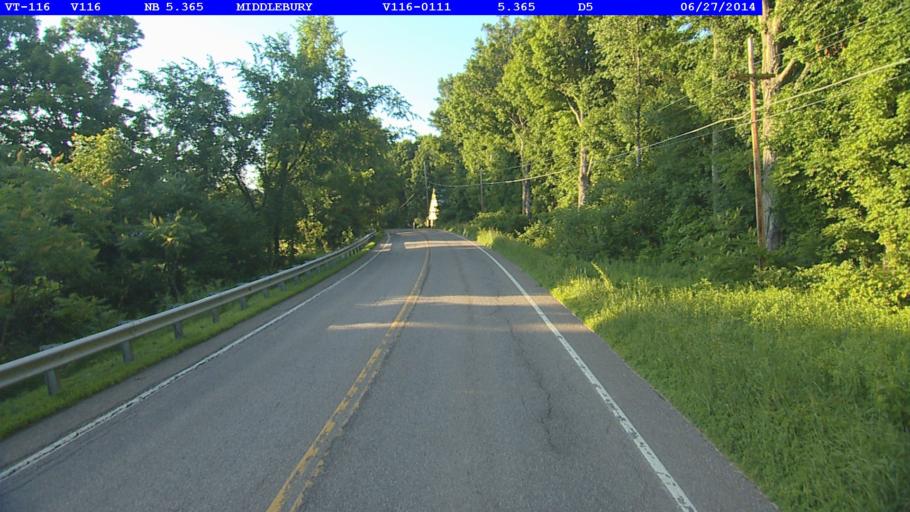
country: US
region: Vermont
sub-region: Addison County
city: Middlebury (village)
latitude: 44.0374
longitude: -73.0910
